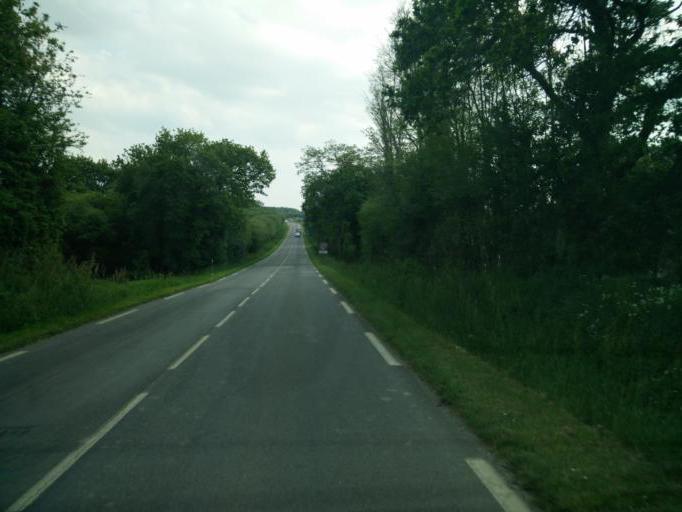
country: FR
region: Brittany
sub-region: Departement du Morbihan
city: Queven
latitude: 47.7678
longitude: -3.4244
